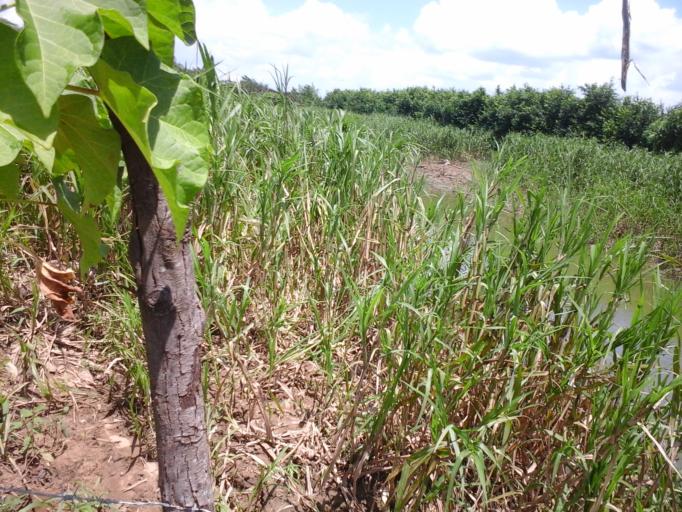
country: CO
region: Bolivar
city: Mahates
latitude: 10.1650
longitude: -75.2749
